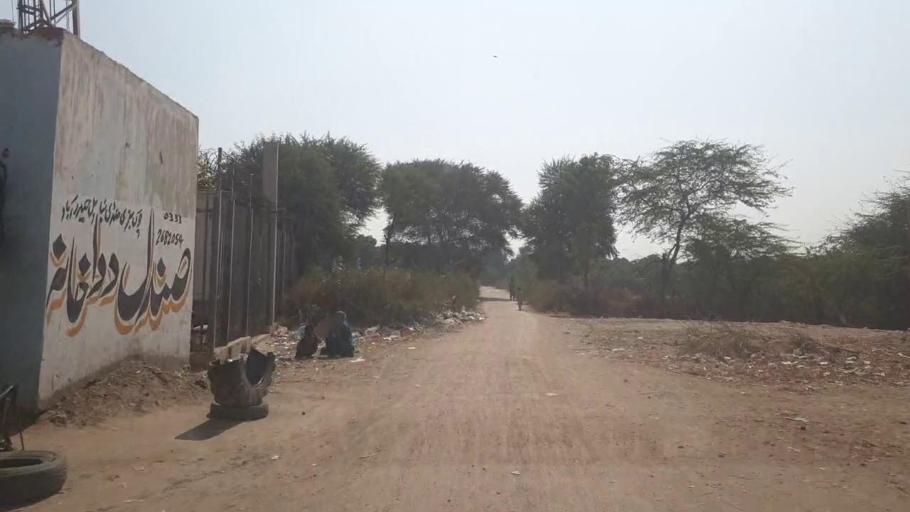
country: PK
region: Sindh
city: Tando Allahyar
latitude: 25.4895
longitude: 68.8481
